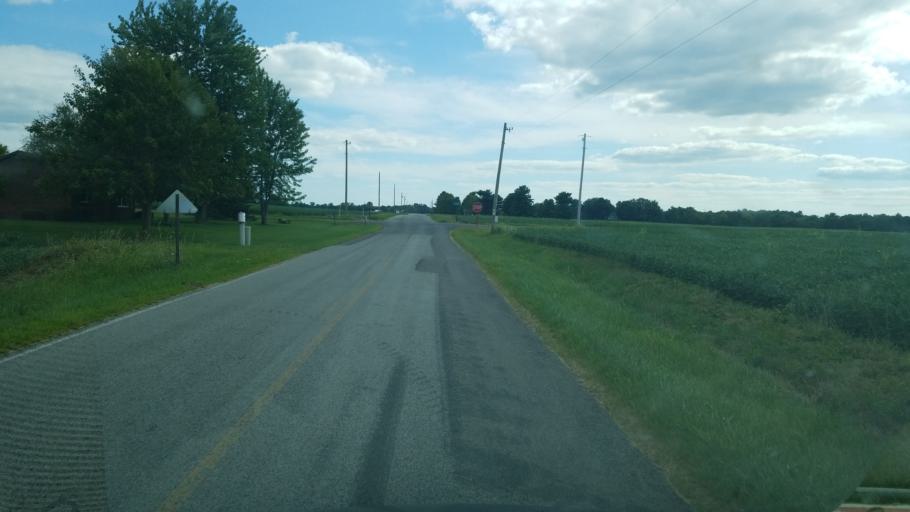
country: US
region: Ohio
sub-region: Champaign County
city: Saint Paris
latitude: 40.1972
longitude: -83.9433
